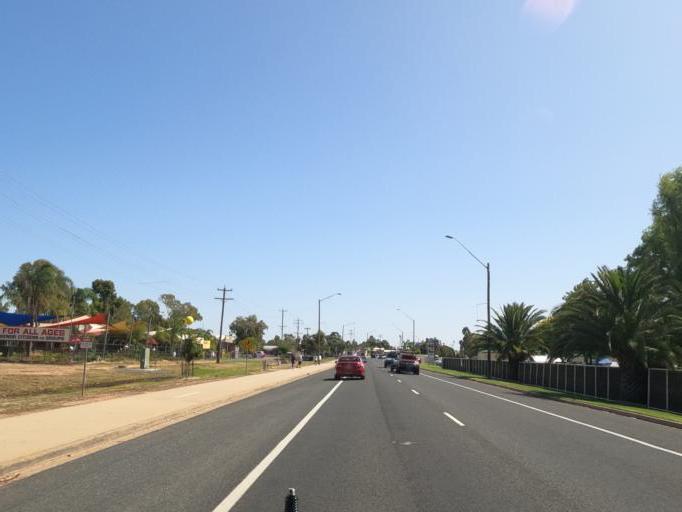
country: AU
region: New South Wales
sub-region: Corowa Shire
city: Mulwala
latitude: -35.9966
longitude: 146.0008
